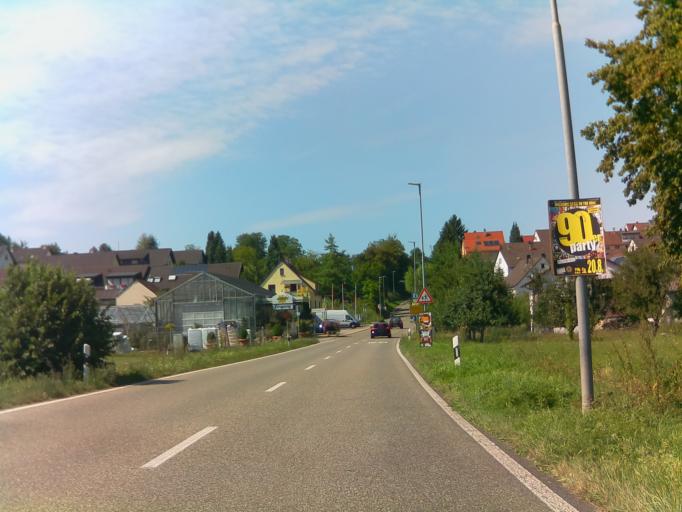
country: DE
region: Baden-Wuerttemberg
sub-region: Karlsruhe Region
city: Oberderdingen
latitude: 49.0997
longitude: 8.7440
